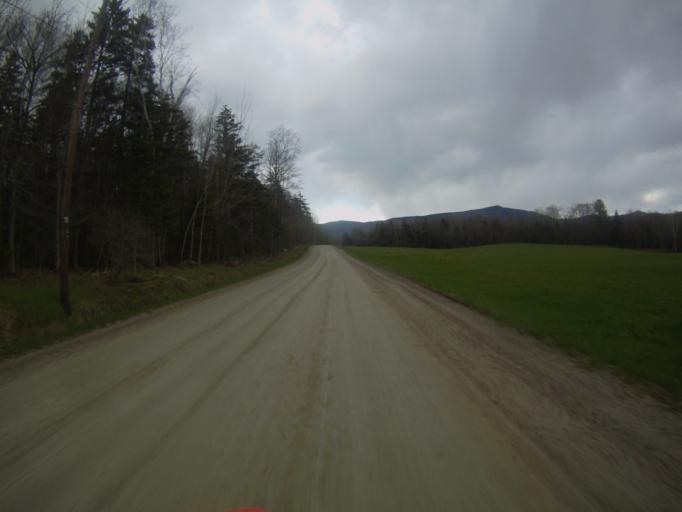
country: US
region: Vermont
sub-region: Addison County
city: Bristol
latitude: 44.0588
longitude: -73.0151
